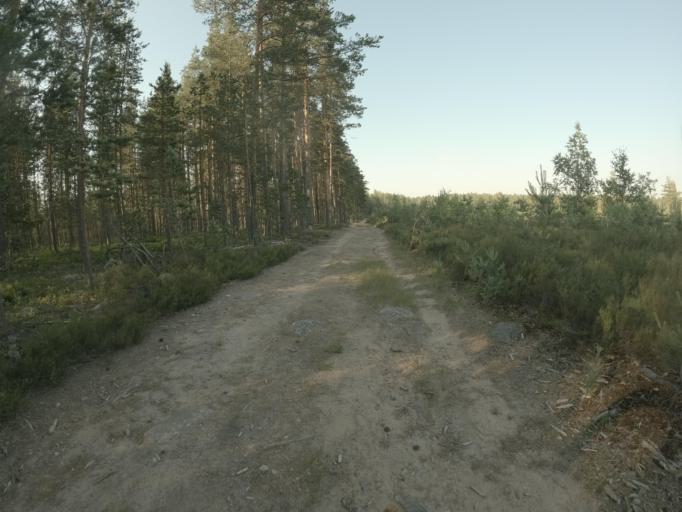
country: RU
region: Leningrad
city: Yakovlevo
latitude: 60.4463
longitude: 29.2424
